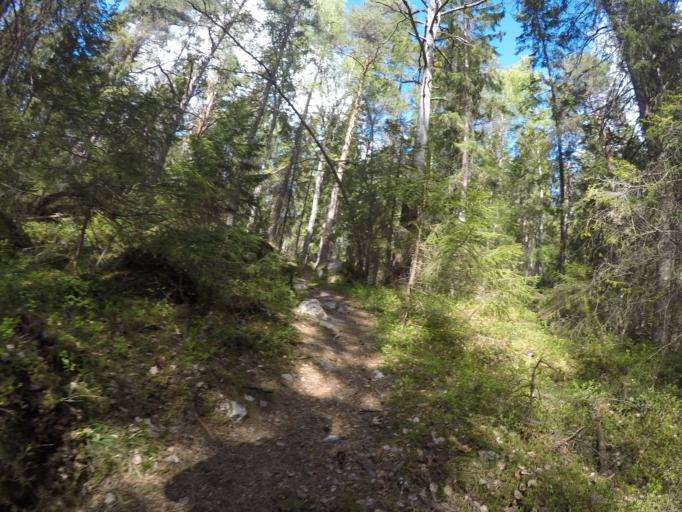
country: SE
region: Soedermanland
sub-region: Eskilstuna Kommun
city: Hallbybrunn
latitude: 59.3537
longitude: 16.4015
